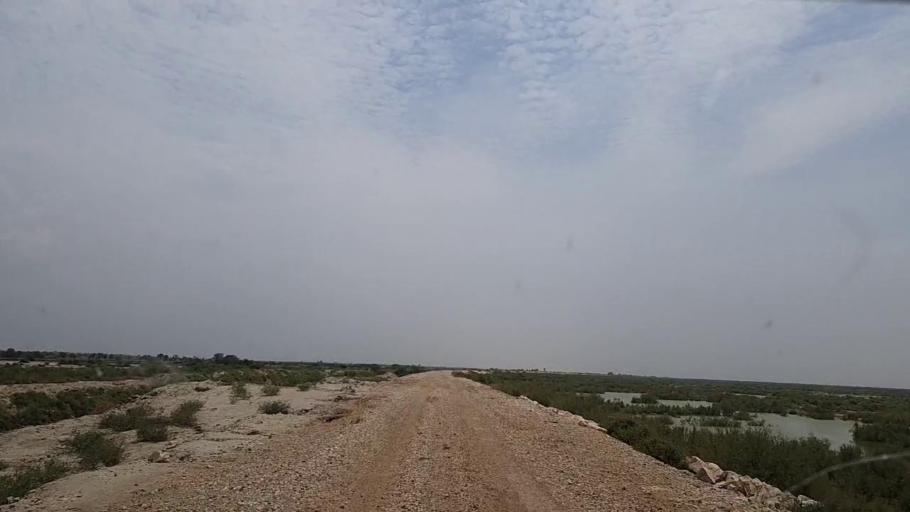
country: PK
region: Sindh
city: Phulji
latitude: 26.8721
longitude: 67.6490
